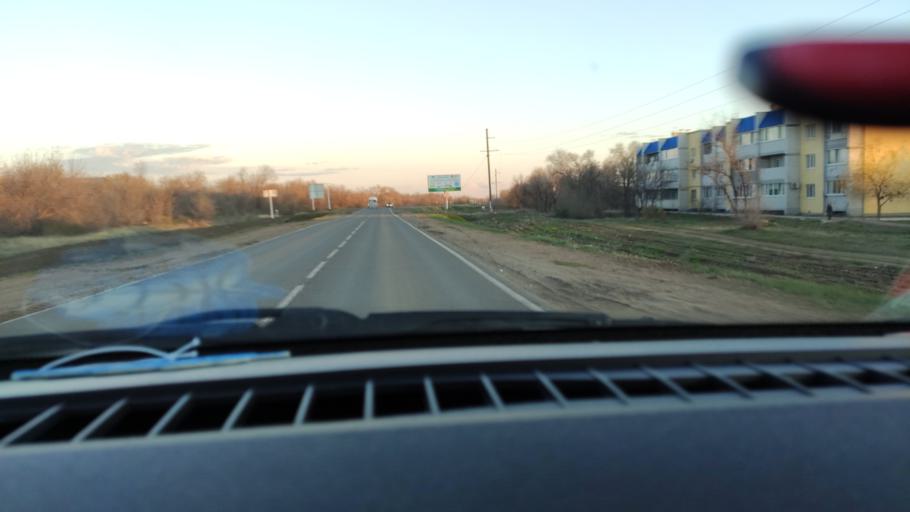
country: RU
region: Saratov
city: Privolzhskiy
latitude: 51.3813
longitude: 46.0422
